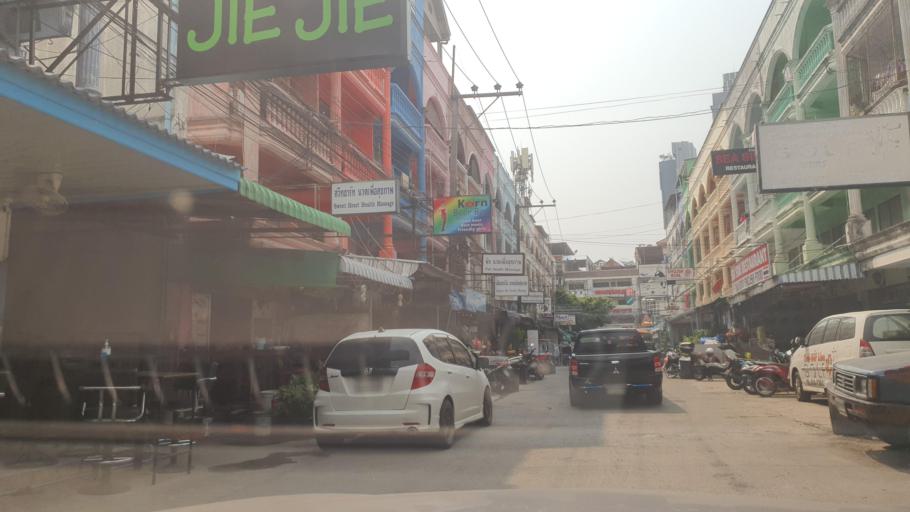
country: TH
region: Chon Buri
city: Phatthaya
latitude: 12.9286
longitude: 100.8859
